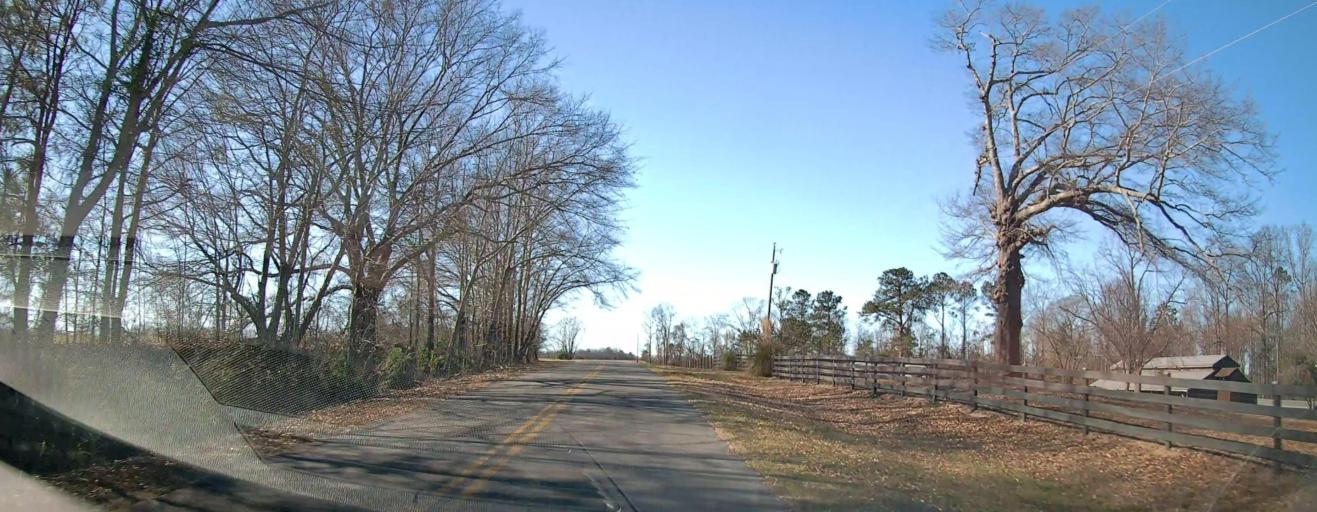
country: US
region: Georgia
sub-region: Taylor County
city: Butler
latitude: 32.6536
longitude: -84.3216
